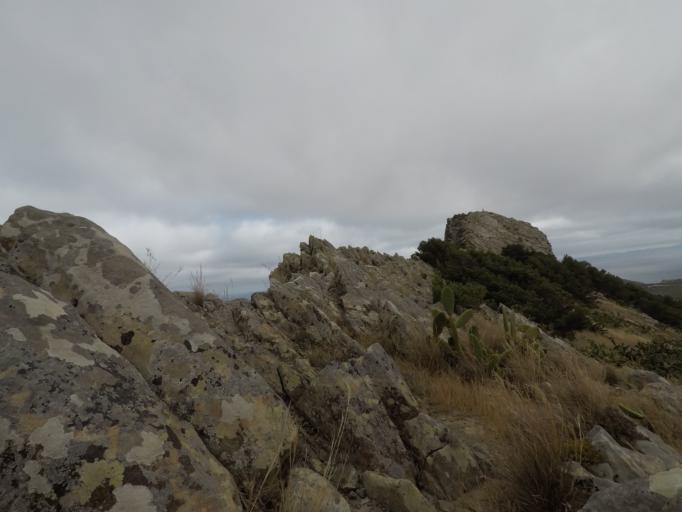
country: PT
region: Madeira
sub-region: Porto Santo
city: Vila de Porto Santo
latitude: 33.0452
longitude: -16.3692
